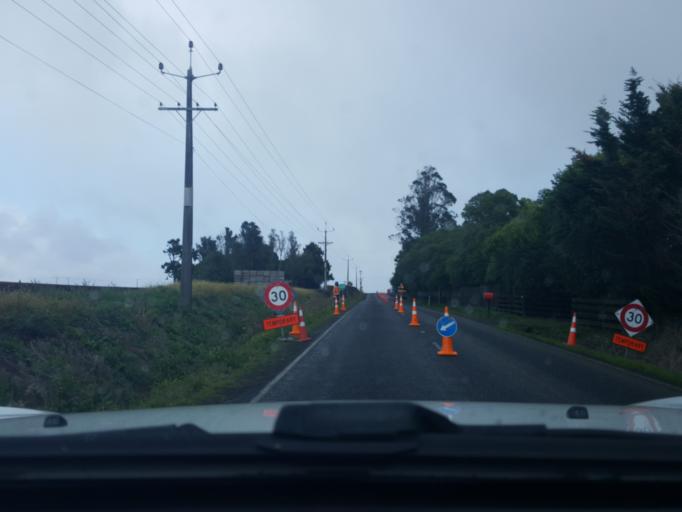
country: NZ
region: Auckland
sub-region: Auckland
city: Pukekohe East
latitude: -37.3090
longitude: 174.9918
